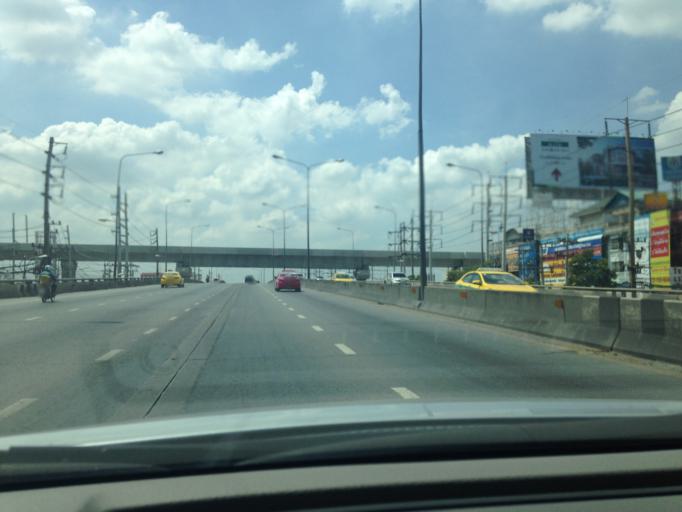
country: TH
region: Phra Nakhon Si Ayutthaya
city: Ban Bang Kadi Pathum Thani
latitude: 13.9865
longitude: 100.6048
